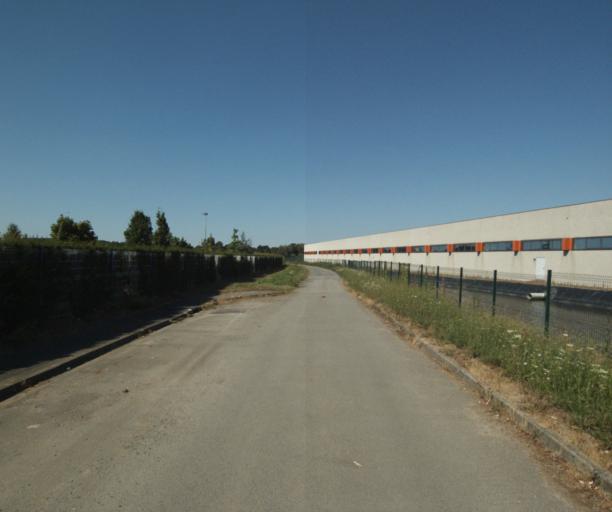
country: FR
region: Nord-Pas-de-Calais
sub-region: Departement du Nord
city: Wervicq-Sud
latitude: 50.7755
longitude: 3.0622
